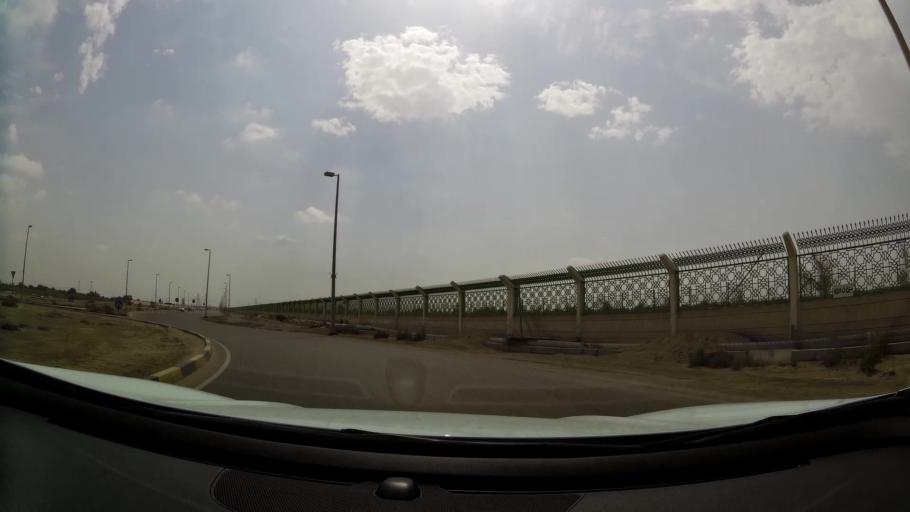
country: AE
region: Abu Dhabi
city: Abu Dhabi
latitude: 24.5350
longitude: 54.6326
